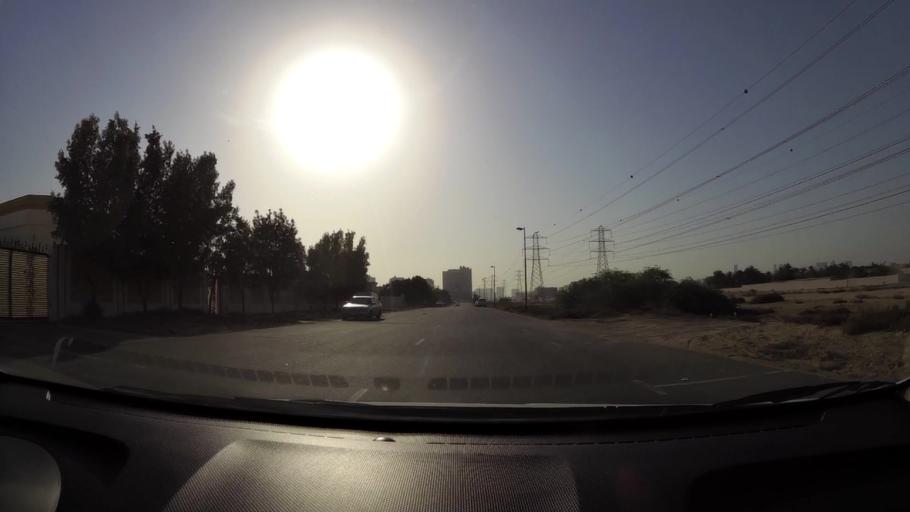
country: AE
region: Ash Shariqah
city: Sharjah
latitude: 25.2723
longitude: 55.3893
